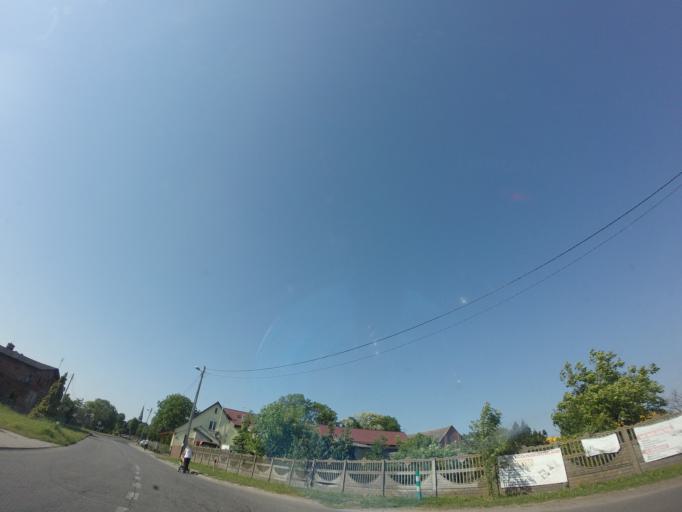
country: PL
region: West Pomeranian Voivodeship
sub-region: Powiat stargardzki
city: Kobylanka
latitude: 53.3216
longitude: 14.8575
